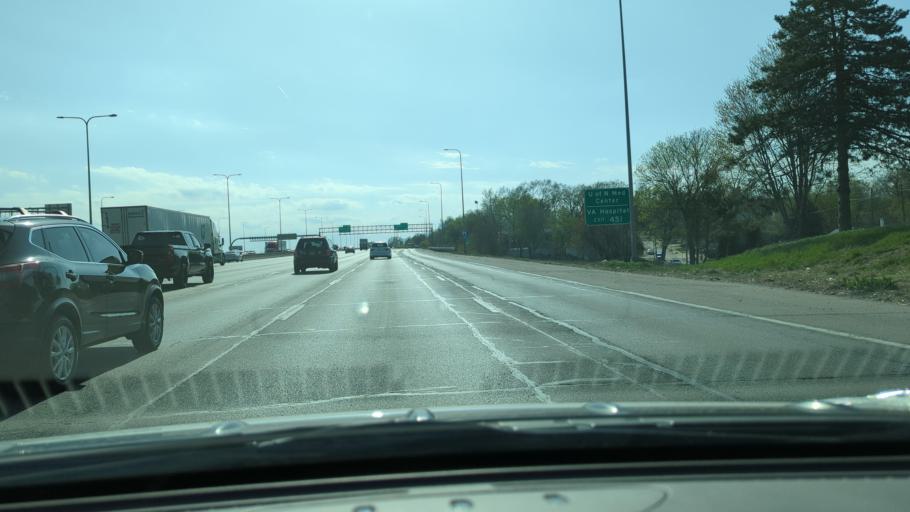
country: US
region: Nebraska
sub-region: Douglas County
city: Omaha
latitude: 41.2263
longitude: -95.9669
